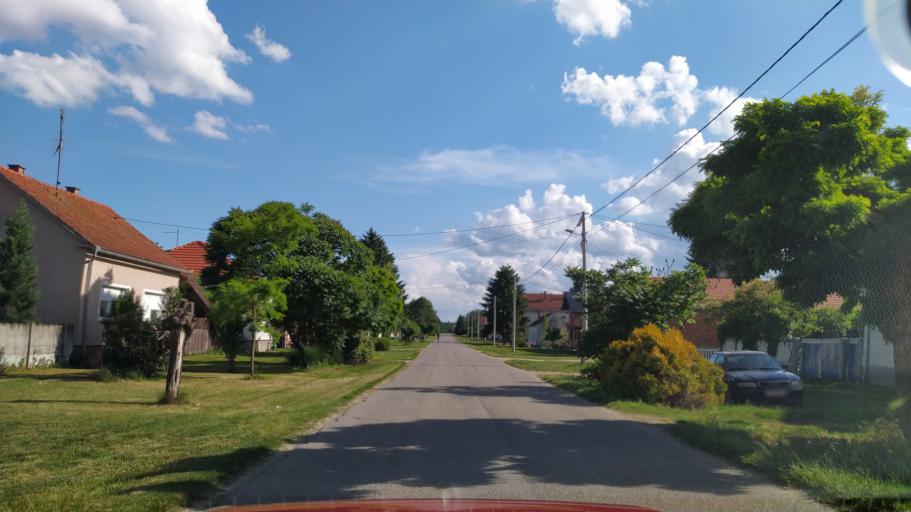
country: HR
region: Virovitick-Podravska
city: Pitomaca
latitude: 45.9600
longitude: 17.2148
